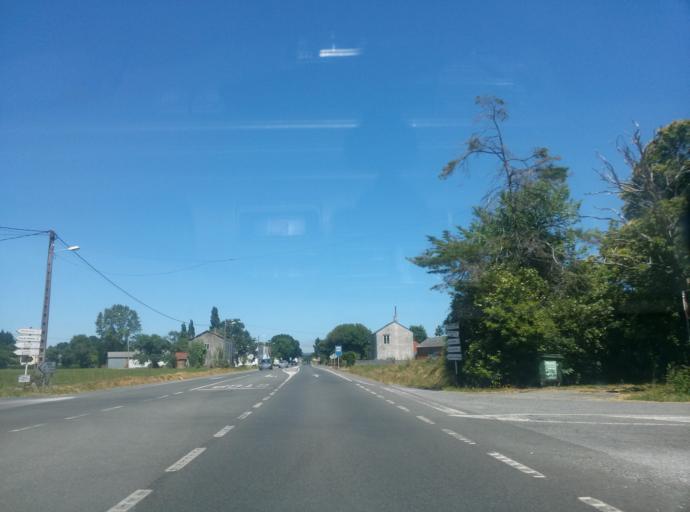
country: ES
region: Galicia
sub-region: Provincia de Lugo
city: Mos
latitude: 43.1744
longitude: -7.4785
